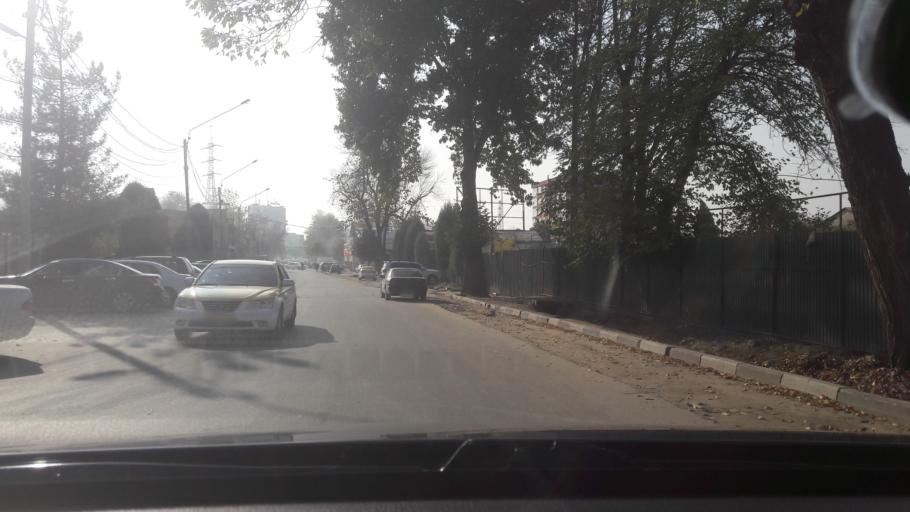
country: TJ
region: Dushanbe
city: Dushanbe
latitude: 38.5627
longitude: 68.7774
